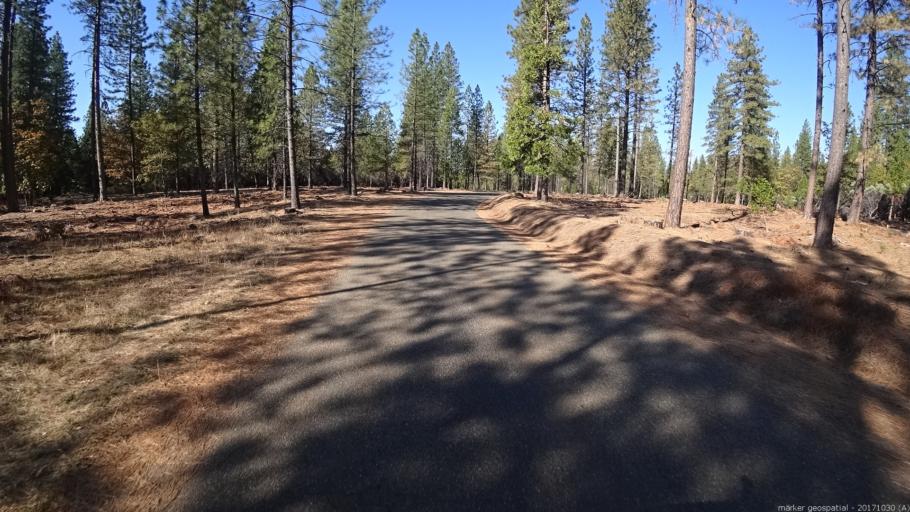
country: US
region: California
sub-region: Shasta County
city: Shingletown
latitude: 40.6112
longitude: -121.8777
